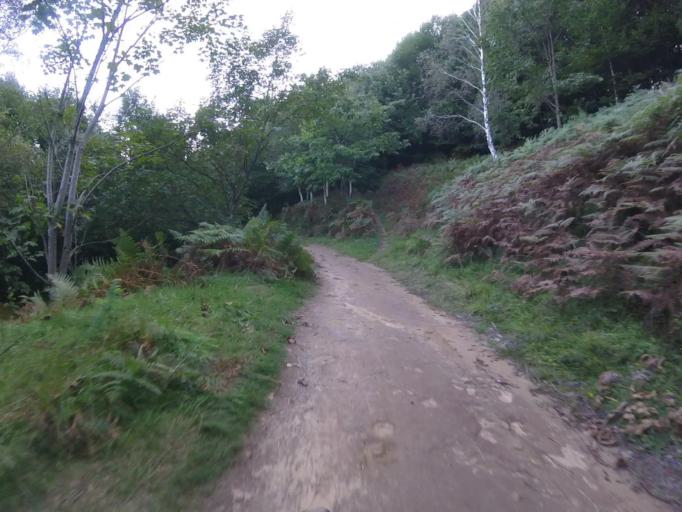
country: ES
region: Basque Country
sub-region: Provincia de Guipuzcoa
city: Fuenterrabia
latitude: 43.3646
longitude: -1.8247
